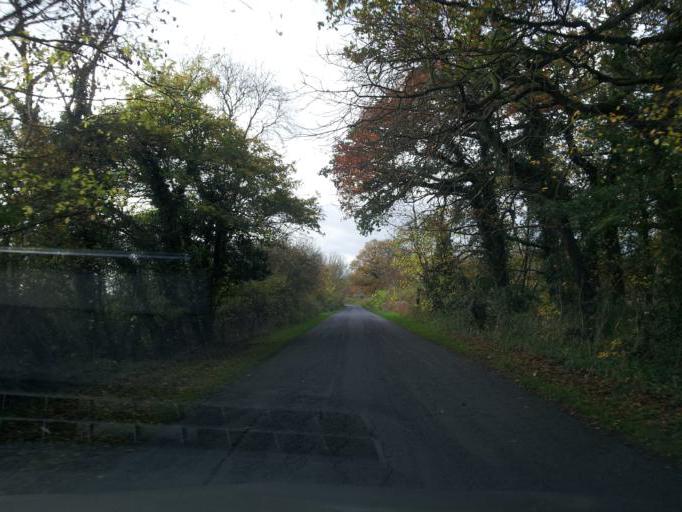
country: GB
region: England
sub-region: Lincolnshire
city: Long Bennington
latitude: 52.9847
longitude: -0.7802
